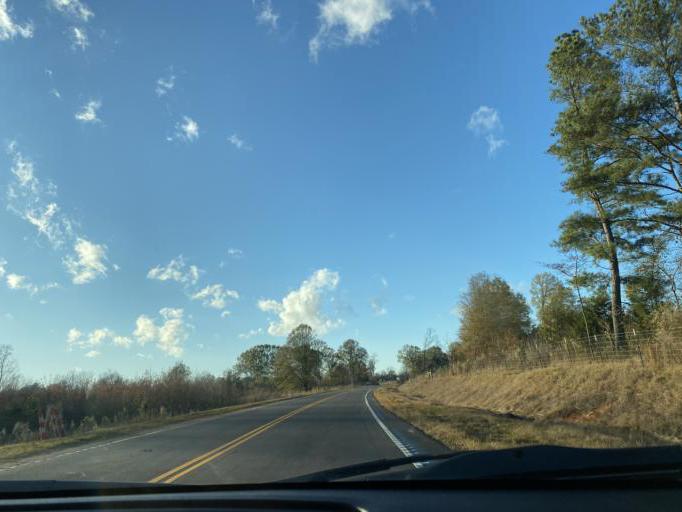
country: US
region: South Carolina
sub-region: York County
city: Clover
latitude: 35.1295
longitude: -81.2301
